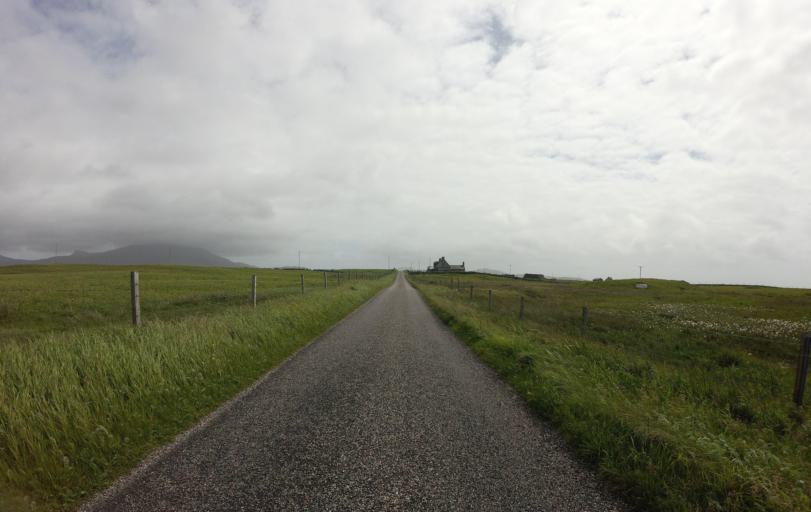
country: GB
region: Scotland
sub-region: Eilean Siar
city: Isle of South Uist
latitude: 57.2758
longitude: -7.4097
